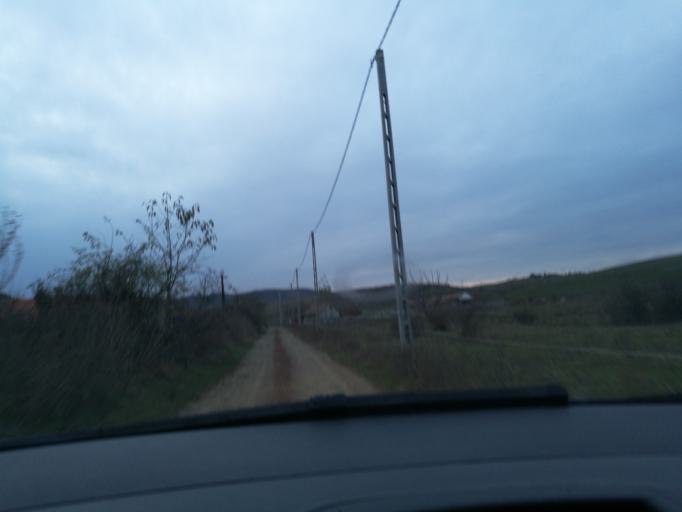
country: HU
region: Nograd
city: Bujak
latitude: 47.8656
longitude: 19.5625
